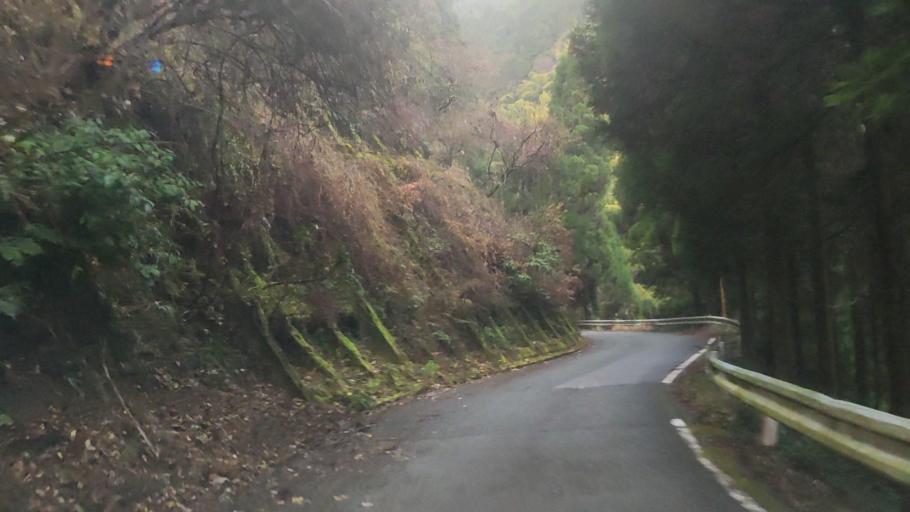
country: JP
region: Kumamoto
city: Matsubase
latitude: 32.5917
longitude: 130.8858
